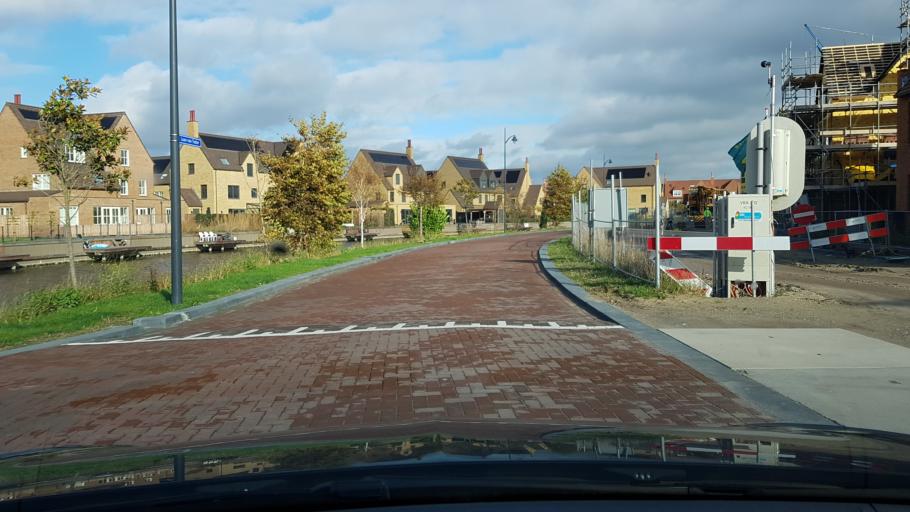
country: NL
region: North Holland
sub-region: Gemeente Haarlemmermeer
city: Hoofddorp
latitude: 52.2922
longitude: 4.6556
